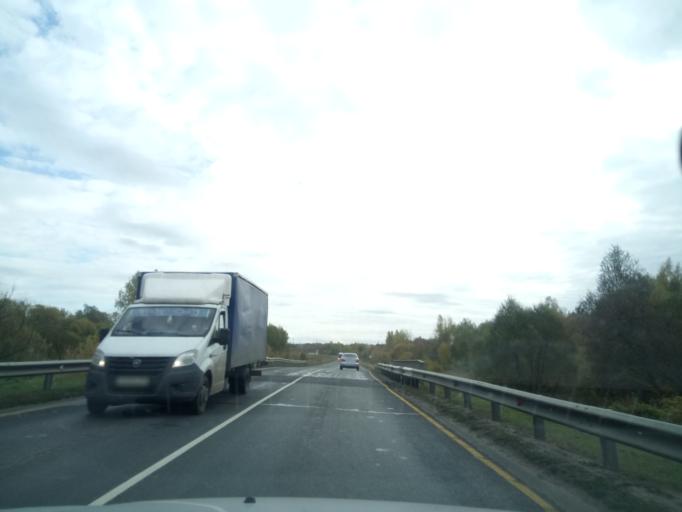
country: RU
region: Nizjnij Novgorod
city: Lukoyanov
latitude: 55.0554
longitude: 44.3693
